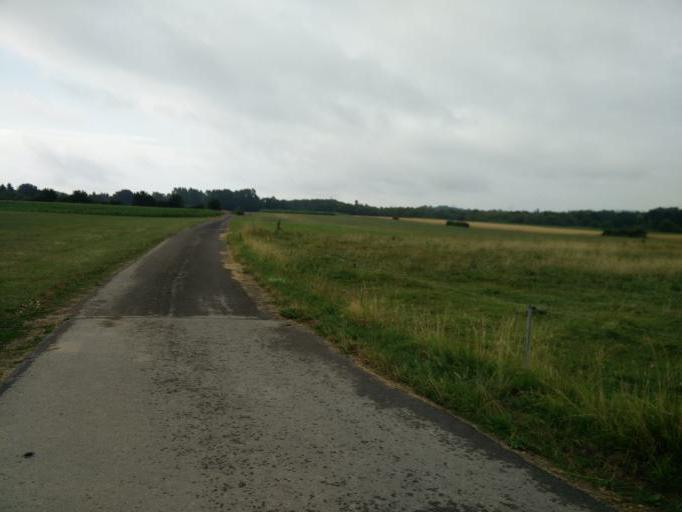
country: LU
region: Luxembourg
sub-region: Canton de Capellen
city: Mamer
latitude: 49.6356
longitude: 6.0392
